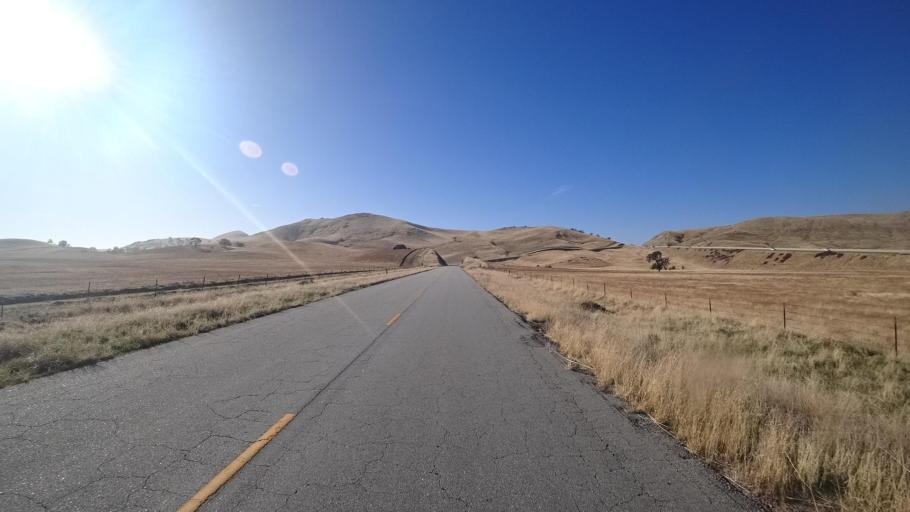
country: US
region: California
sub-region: Kern County
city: Bear Valley Springs
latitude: 35.2644
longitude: -118.6656
